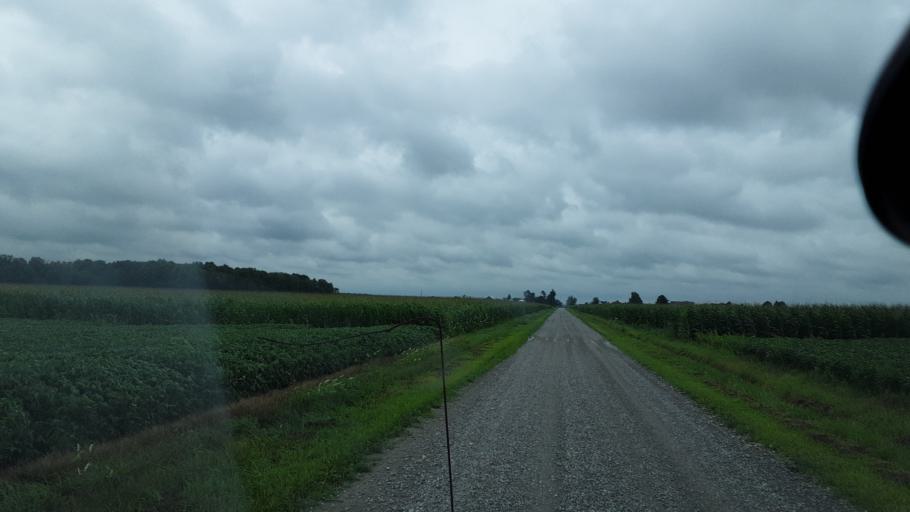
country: US
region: Indiana
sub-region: Wells County
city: Ossian
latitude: 40.8492
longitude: -85.0820
